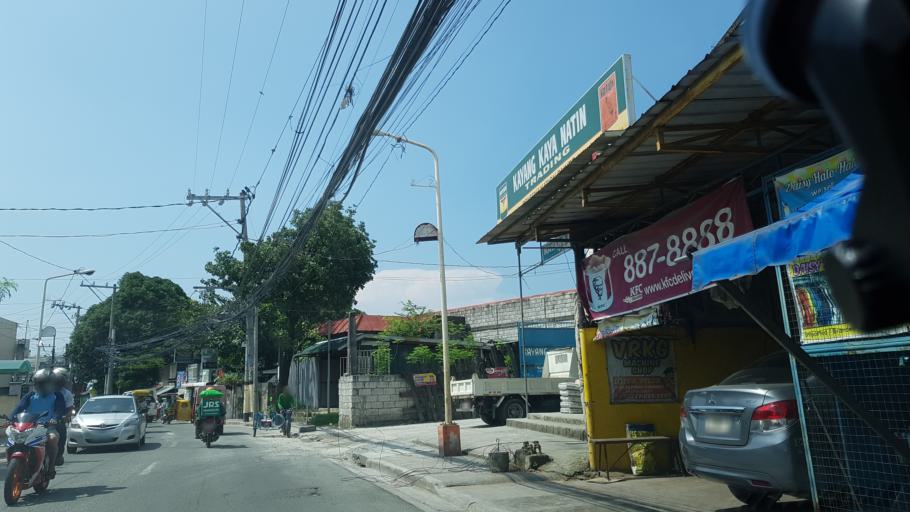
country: PH
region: Calabarzon
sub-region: Province of Rizal
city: Las Pinas
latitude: 14.4674
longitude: 120.9821
